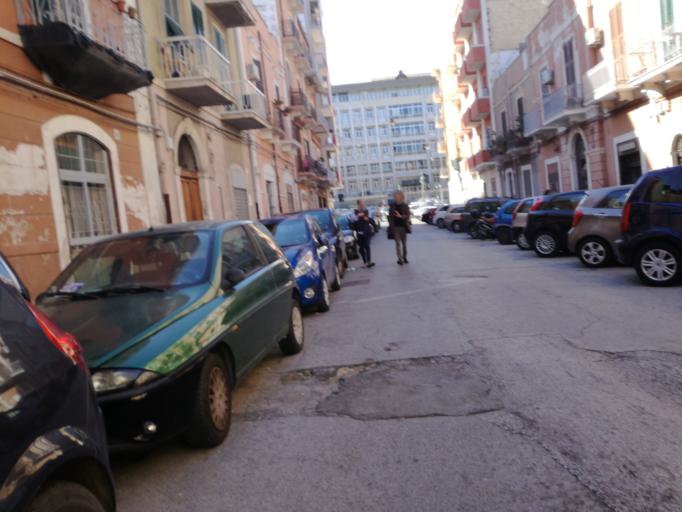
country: IT
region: Apulia
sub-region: Provincia di Bari
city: Bari
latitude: 41.1240
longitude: 16.8582
